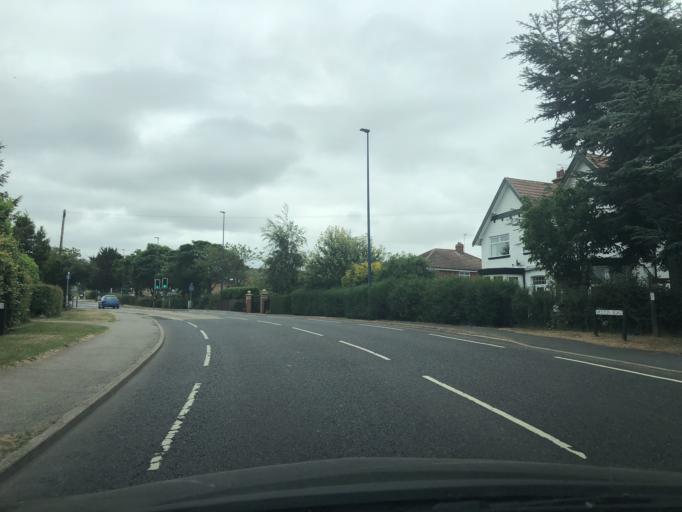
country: GB
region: England
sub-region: North Yorkshire
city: Filey
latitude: 54.2063
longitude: -0.3012
